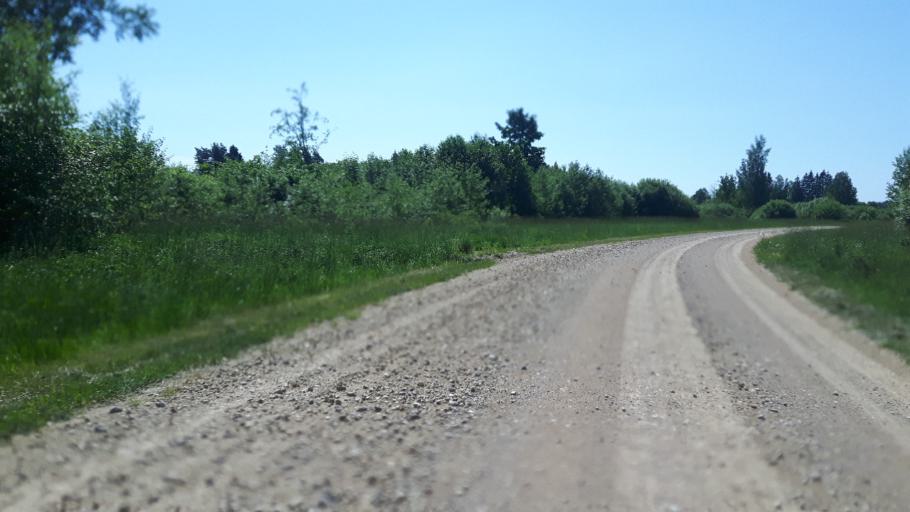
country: EE
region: Paernumaa
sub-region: Vaendra vald (alev)
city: Vandra
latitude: 58.5607
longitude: 24.9530
